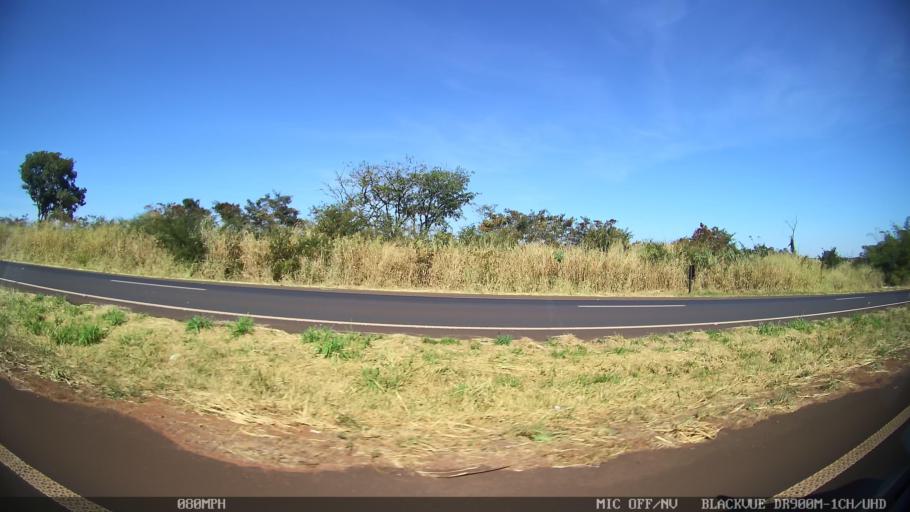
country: BR
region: Sao Paulo
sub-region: Barretos
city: Barretos
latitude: -20.5193
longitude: -48.5754
